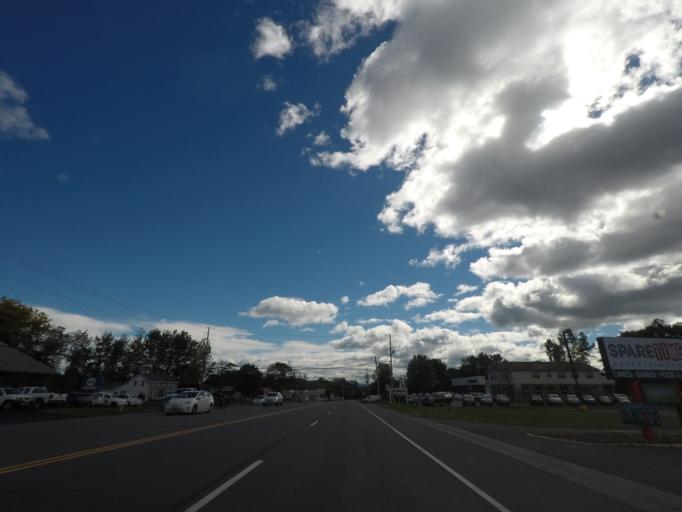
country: US
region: New York
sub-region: Saratoga County
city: Country Knolls
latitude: 42.8591
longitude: -73.7638
